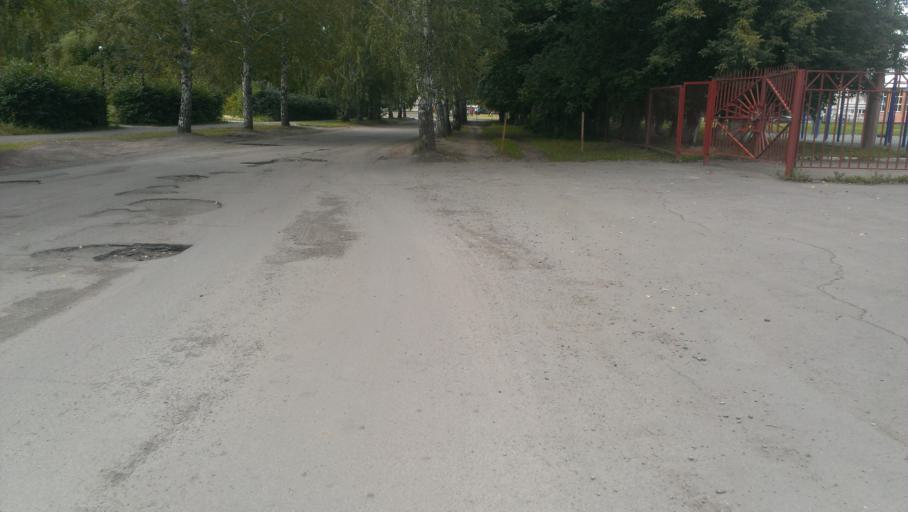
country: RU
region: Altai Krai
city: Yuzhnyy
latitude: 53.2526
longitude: 83.6926
